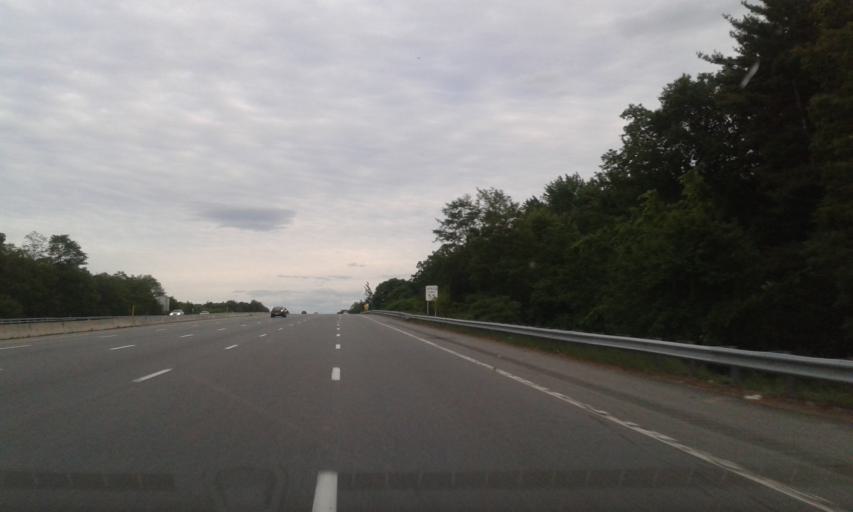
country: US
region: New Hampshire
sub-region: Hillsborough County
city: Nashua
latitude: 42.7619
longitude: -71.4936
